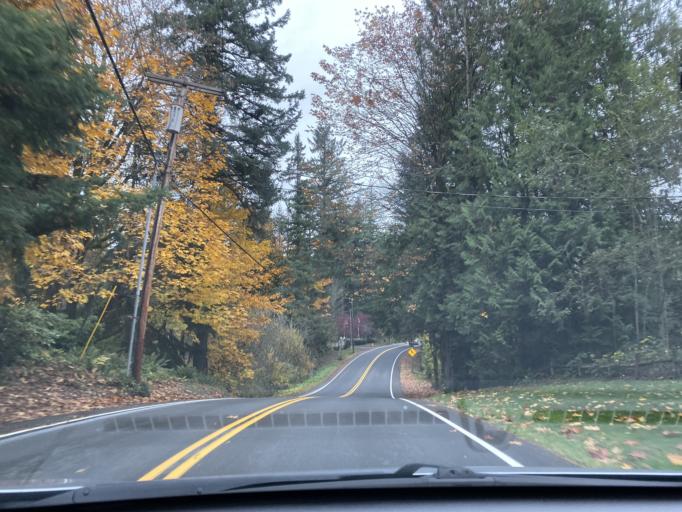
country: US
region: Washington
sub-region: King County
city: Lake Morton-Berrydale
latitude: 47.3016
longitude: -122.1213
